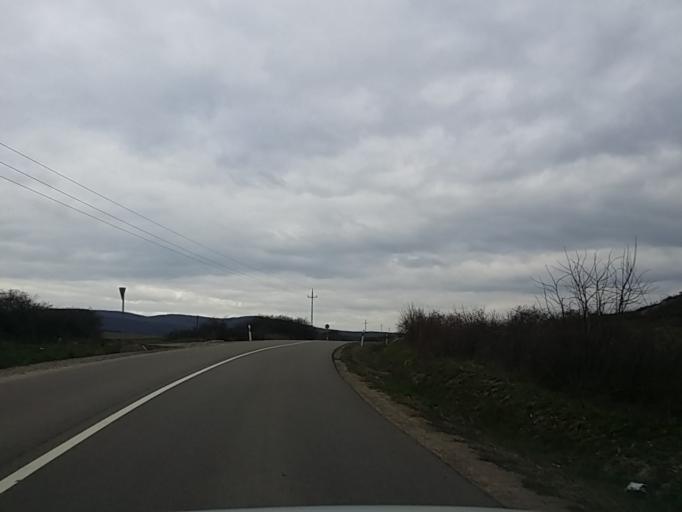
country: HU
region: Heves
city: Verpelet
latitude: 47.8574
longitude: 20.2063
